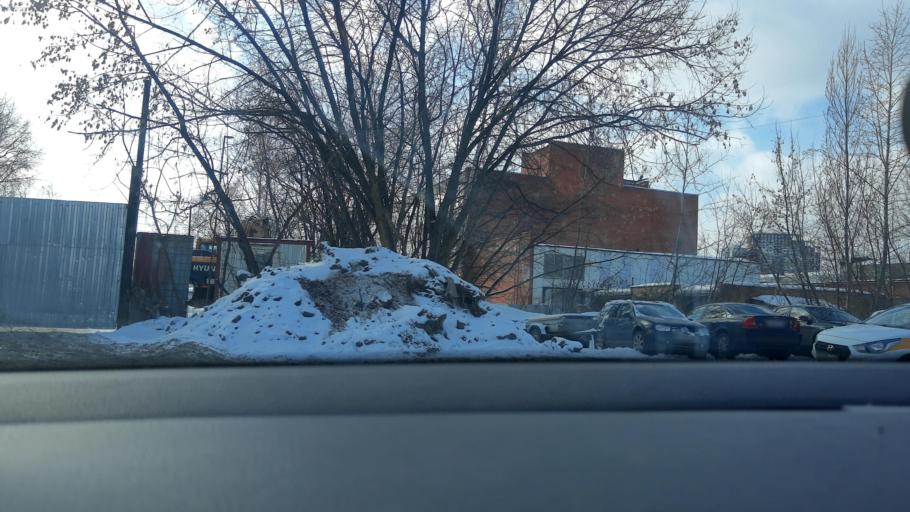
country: RU
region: Moscow
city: Metrogorodok
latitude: 55.8106
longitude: 37.7538
